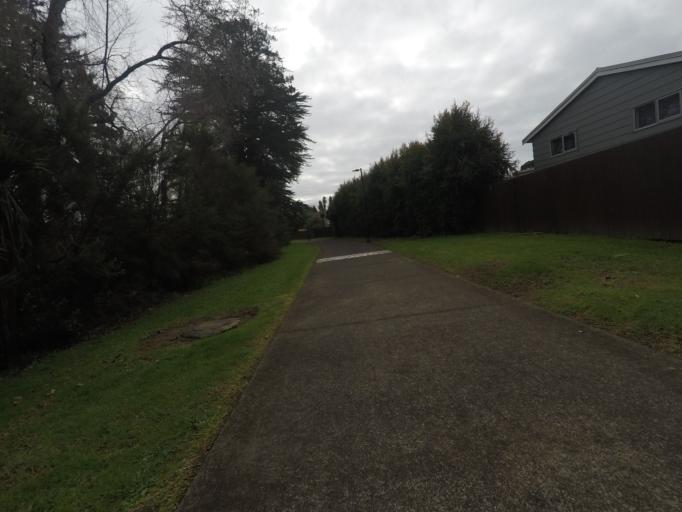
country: NZ
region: Auckland
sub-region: Auckland
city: Waitakere
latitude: -36.9044
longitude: 174.6253
